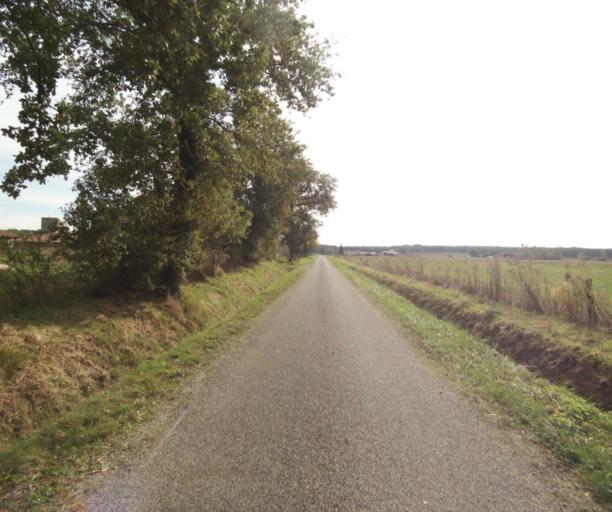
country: FR
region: Midi-Pyrenees
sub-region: Departement du Tarn-et-Garonne
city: Campsas
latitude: 43.8808
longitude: 1.3574
